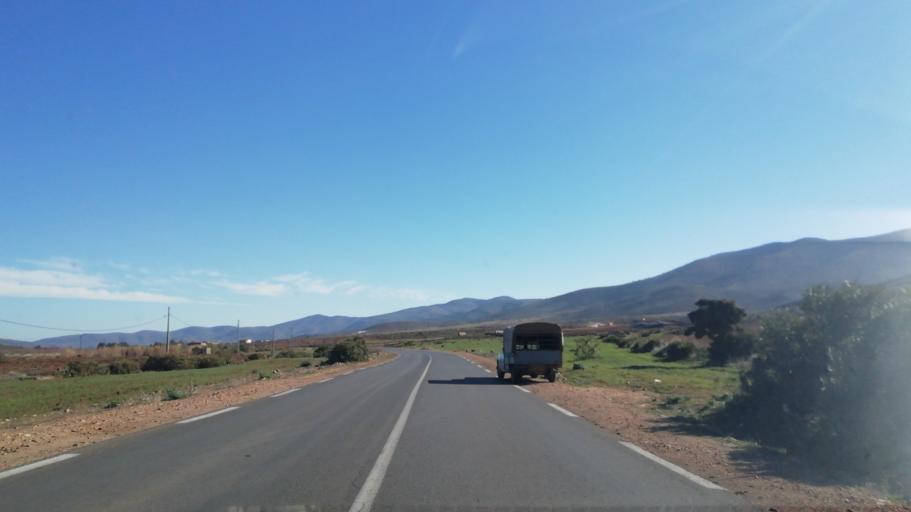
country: DZ
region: Tlemcen
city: Ouled Mimoun
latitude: 34.7751
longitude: -1.1253
